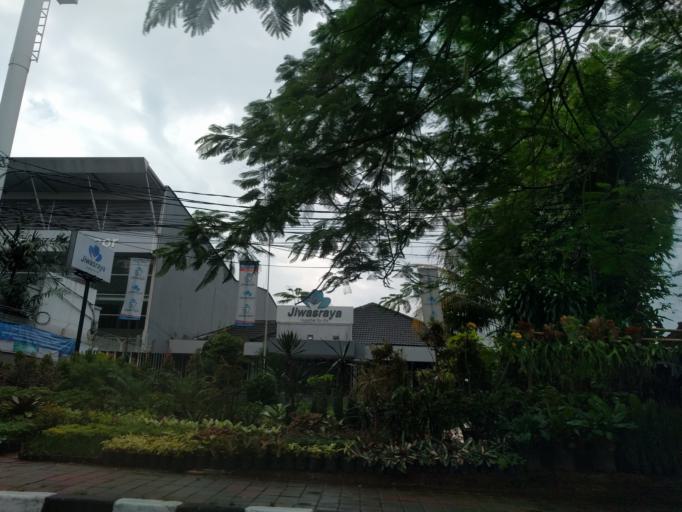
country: ID
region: West Java
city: Bogor
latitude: -6.5851
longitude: 106.8059
